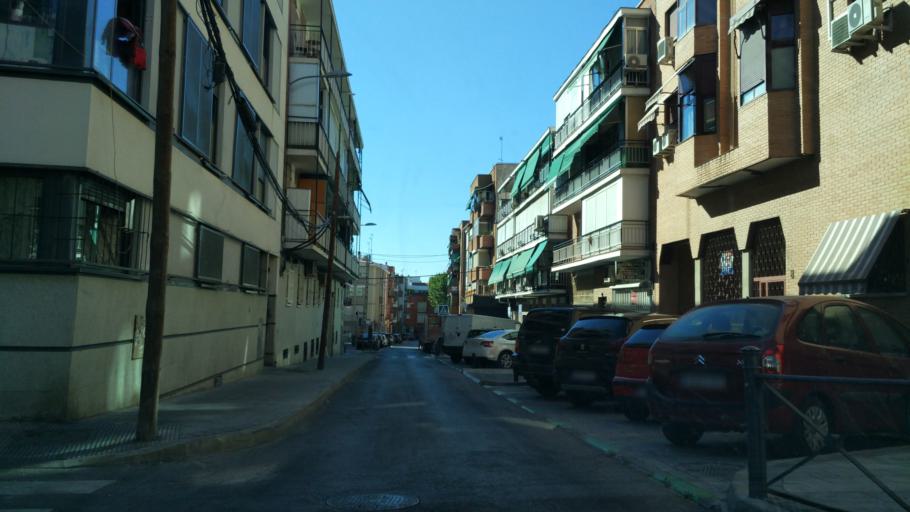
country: ES
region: Madrid
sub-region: Provincia de Madrid
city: Tetuan de las Victorias
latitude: 40.4669
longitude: -3.6990
